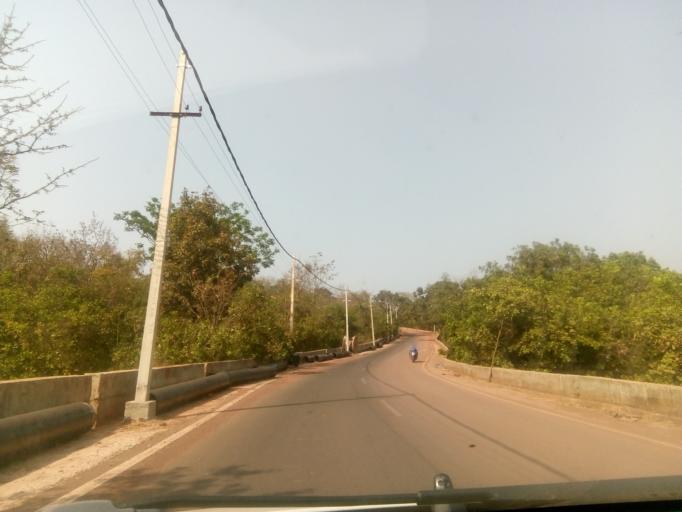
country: IN
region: Goa
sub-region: North Goa
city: Pernem
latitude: 15.7263
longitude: 73.8553
